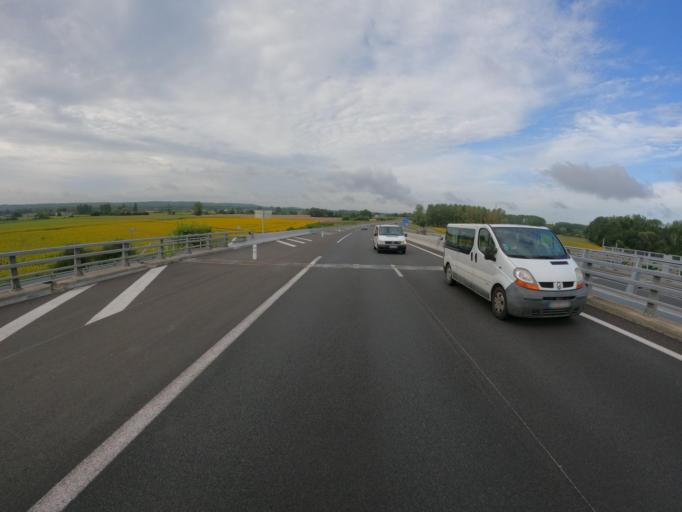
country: FR
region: Centre
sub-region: Departement d'Indre-et-Loire
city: Restigne
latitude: 47.2797
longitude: 0.2772
